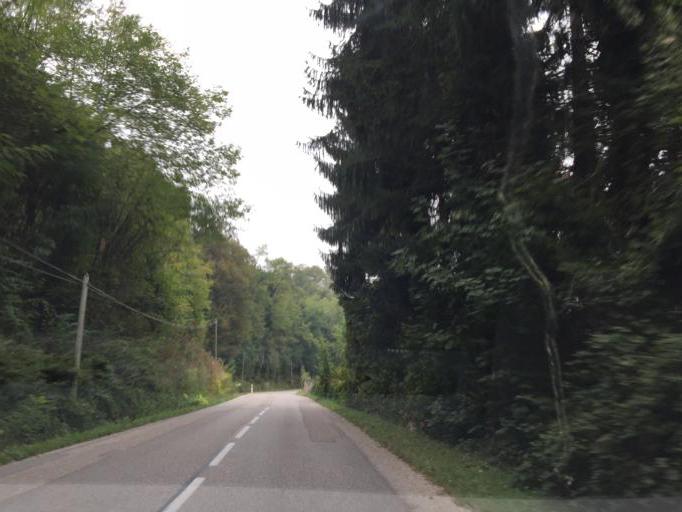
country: FR
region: Rhone-Alpes
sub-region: Departement de l'Isere
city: Saint-Clair-de-la-Tour
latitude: 45.5766
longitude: 5.4812
